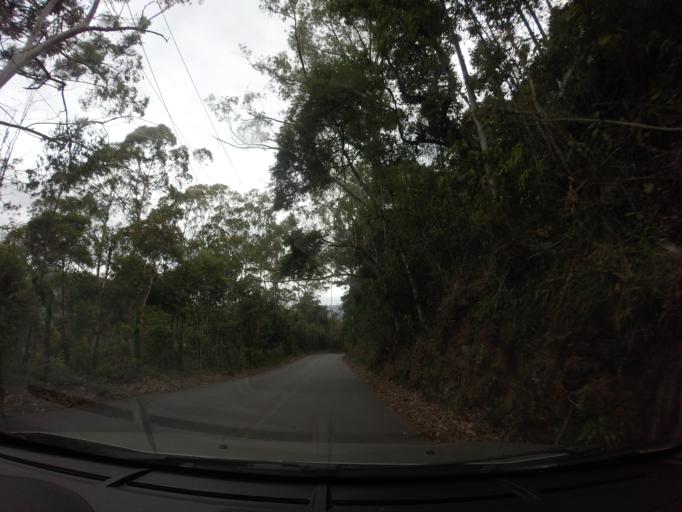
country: BR
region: Sao Paulo
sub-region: Campos Do Jordao
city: Campos do Jordao
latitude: -22.6672
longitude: -45.5960
